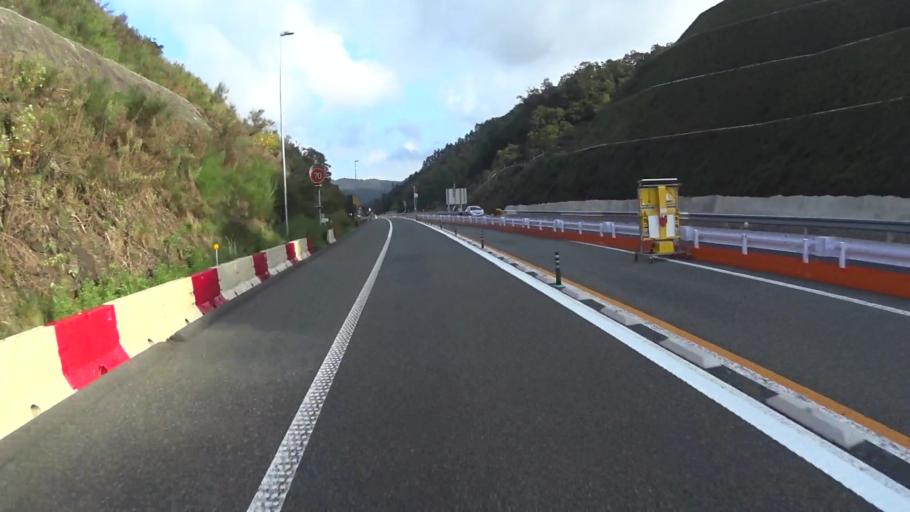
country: JP
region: Kyoto
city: Ayabe
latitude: 35.2834
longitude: 135.3372
